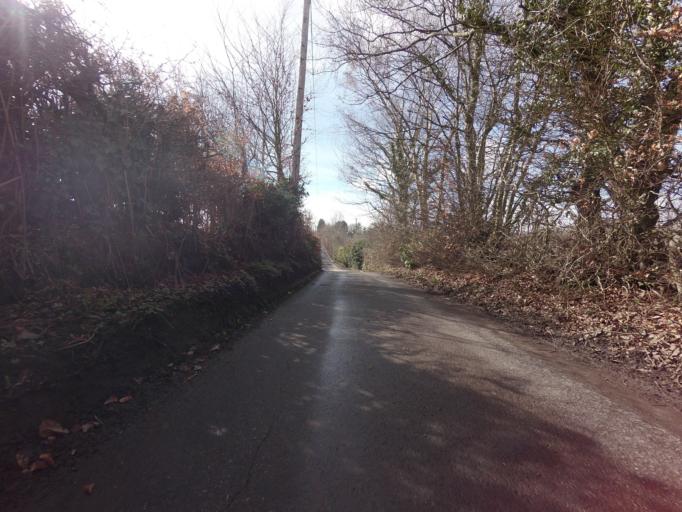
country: GB
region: England
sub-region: Kent
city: Shoreham
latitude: 51.3614
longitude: 0.1527
